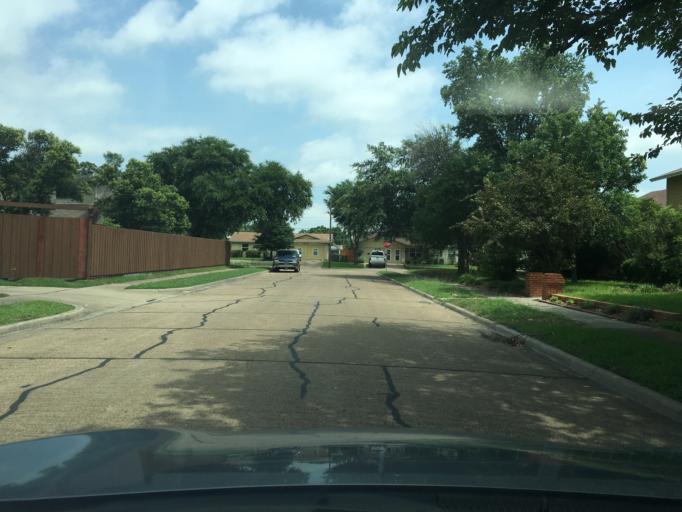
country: US
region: Texas
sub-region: Dallas County
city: Garland
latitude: 32.9228
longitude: -96.6802
